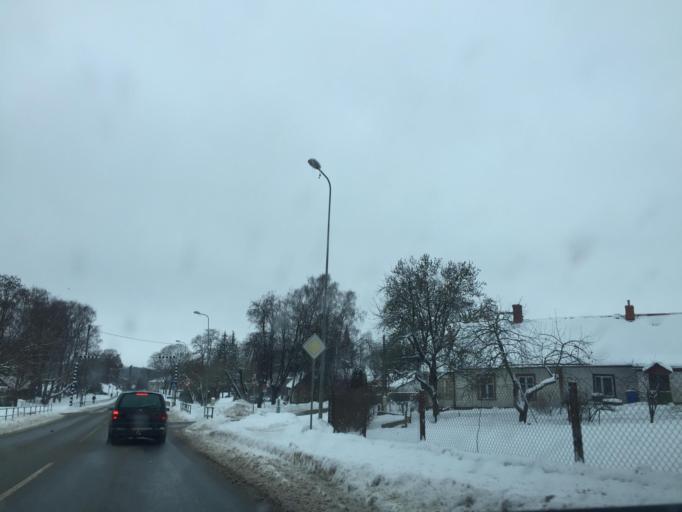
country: LV
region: Smiltene
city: Smiltene
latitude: 57.4209
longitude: 25.9067
